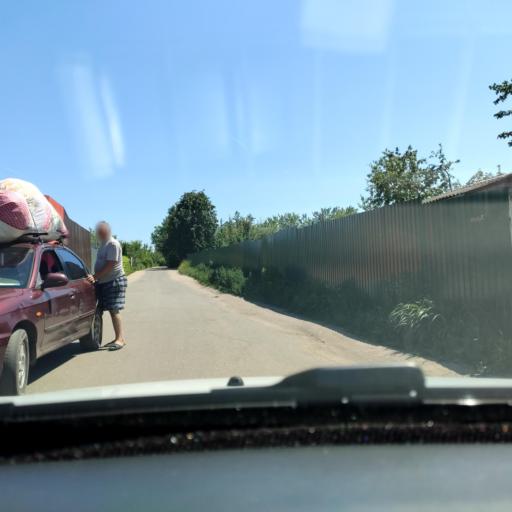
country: RU
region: Voronezj
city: Shilovo
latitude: 51.5898
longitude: 39.1513
